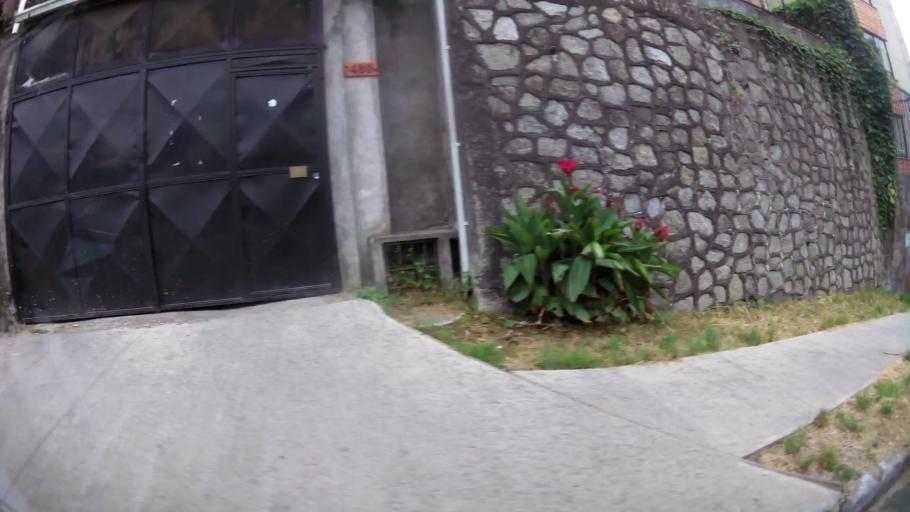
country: CL
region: Biobio
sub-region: Provincia de Concepcion
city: Concepcion
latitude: -36.8336
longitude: -73.0369
